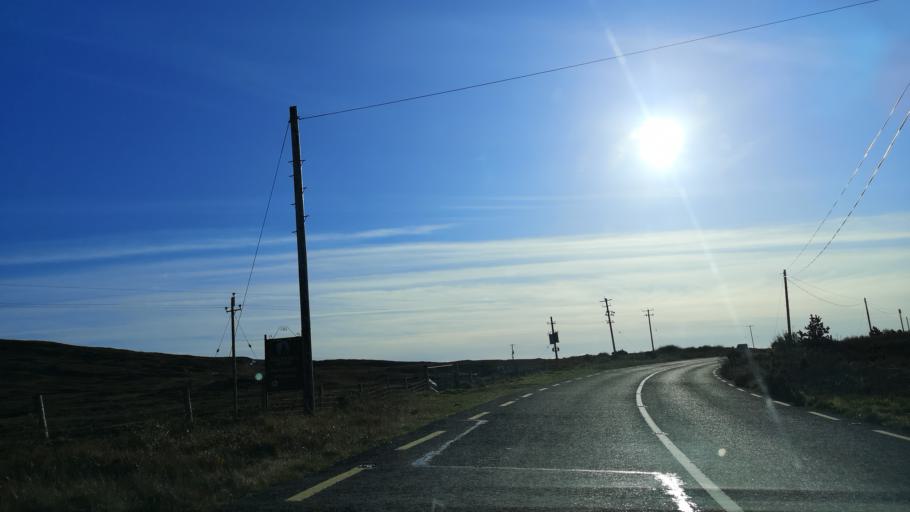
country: IE
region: Connaught
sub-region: County Galway
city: Clifden
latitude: 53.5316
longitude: -10.0389
